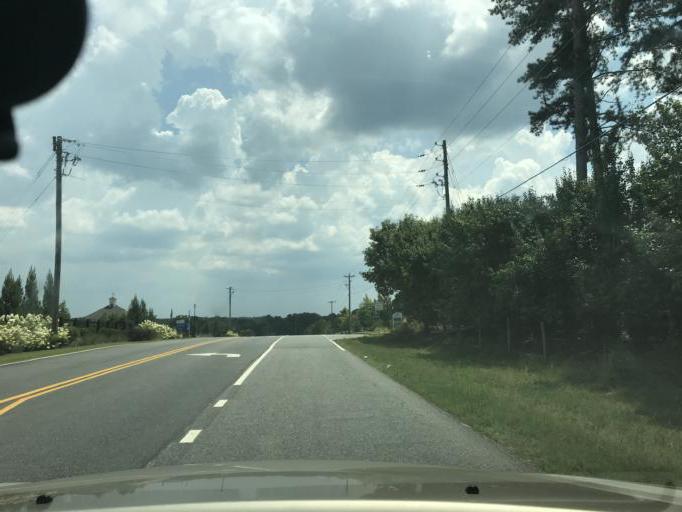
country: US
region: Georgia
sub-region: Forsyth County
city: Cumming
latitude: 34.2339
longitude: -84.2050
